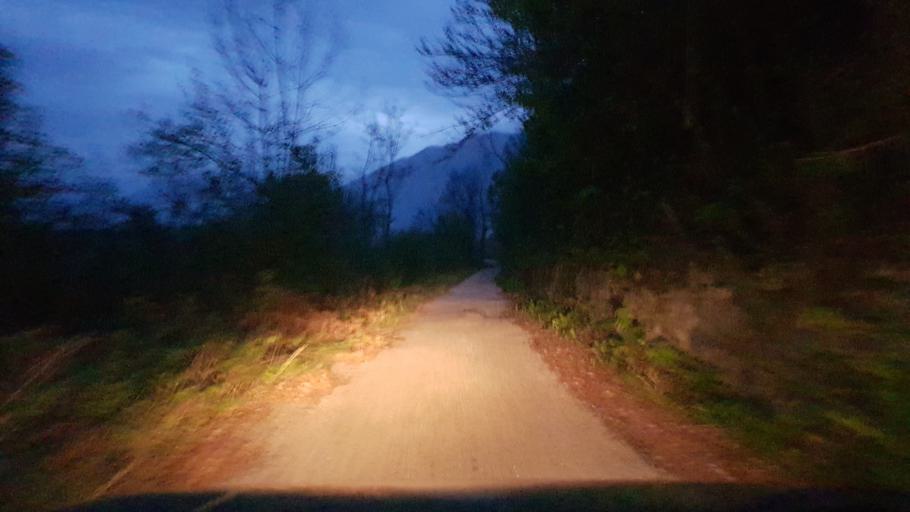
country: IT
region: Friuli Venezia Giulia
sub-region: Provincia di Udine
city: Taipana
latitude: 46.2570
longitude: 13.3522
